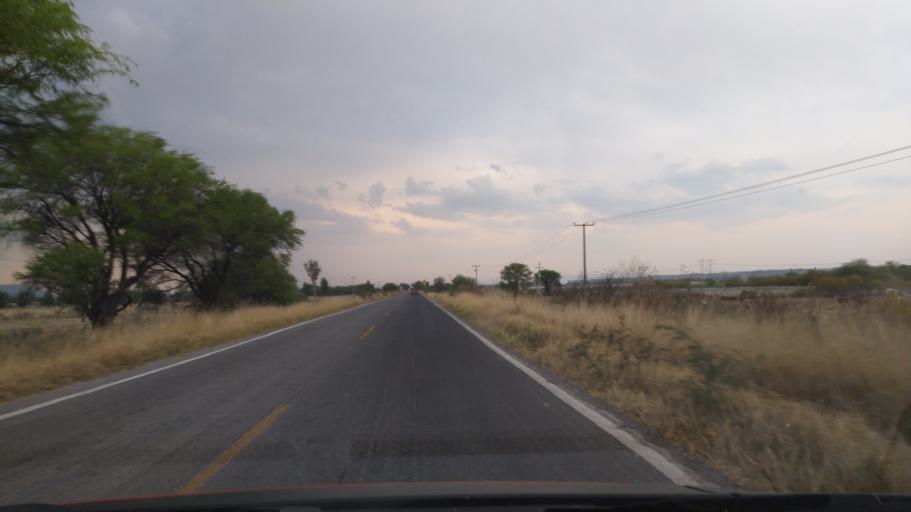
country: MX
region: Guanajuato
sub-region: San Francisco del Rincon
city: San Ignacio de Hidalgo
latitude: 20.8355
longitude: -101.8989
